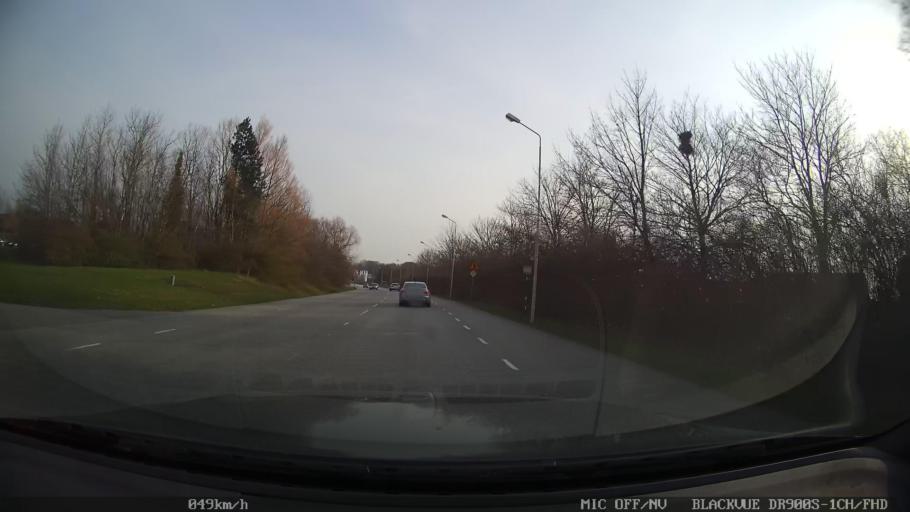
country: SE
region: Skane
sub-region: Ystads Kommun
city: Ystad
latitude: 55.4410
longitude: 13.8072
